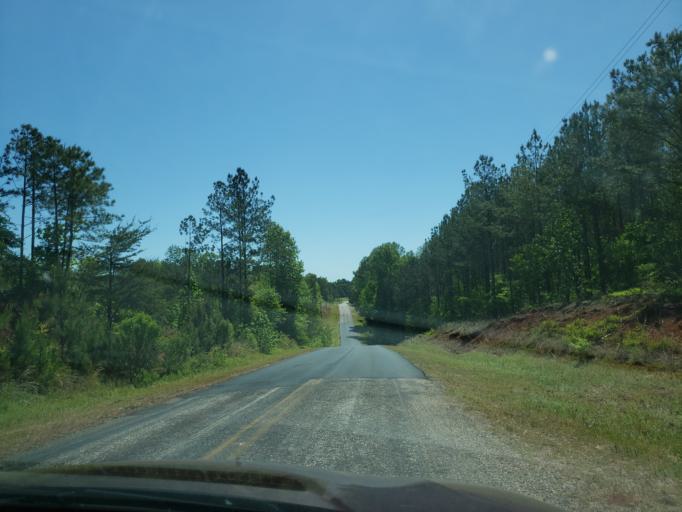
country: US
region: Alabama
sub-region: Tallapoosa County
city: Dadeville
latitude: 32.7007
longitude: -85.8660
